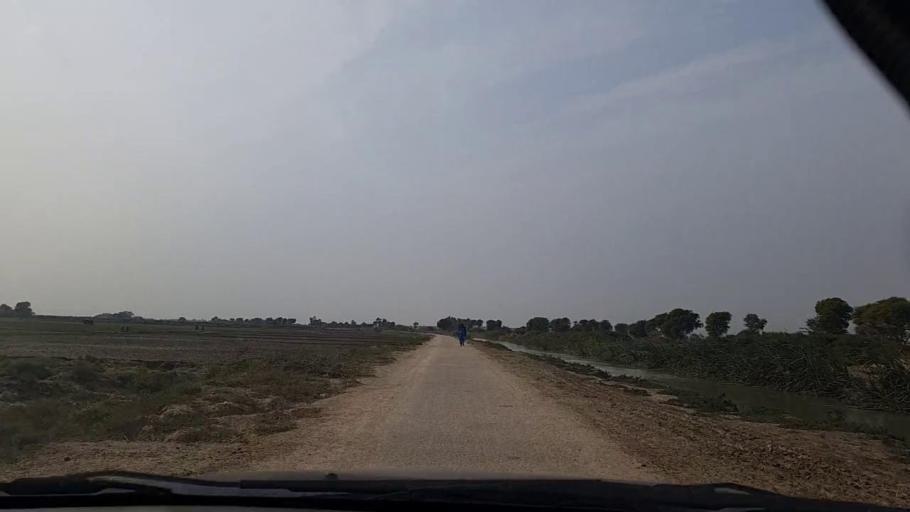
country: PK
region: Sindh
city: Thatta
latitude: 24.5779
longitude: 67.8880
